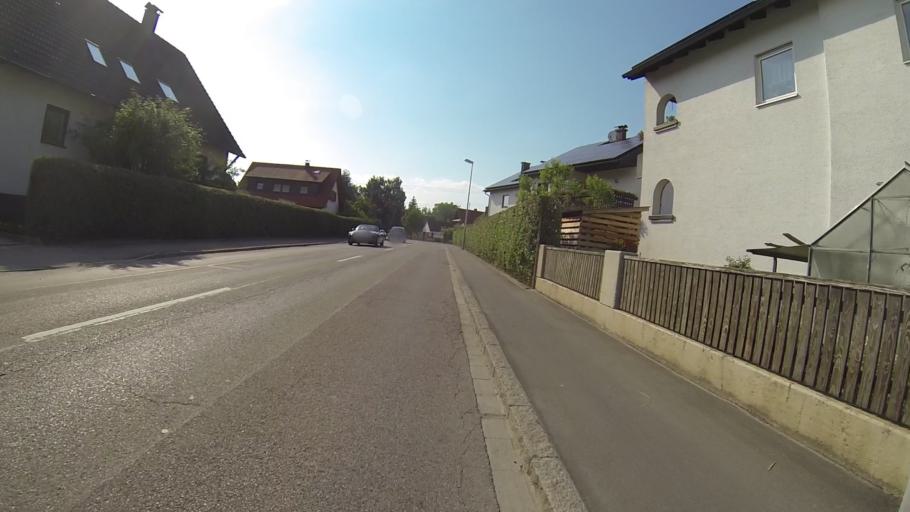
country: DE
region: Bavaria
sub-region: Swabia
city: Holzheim
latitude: 48.3861
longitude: 10.0747
